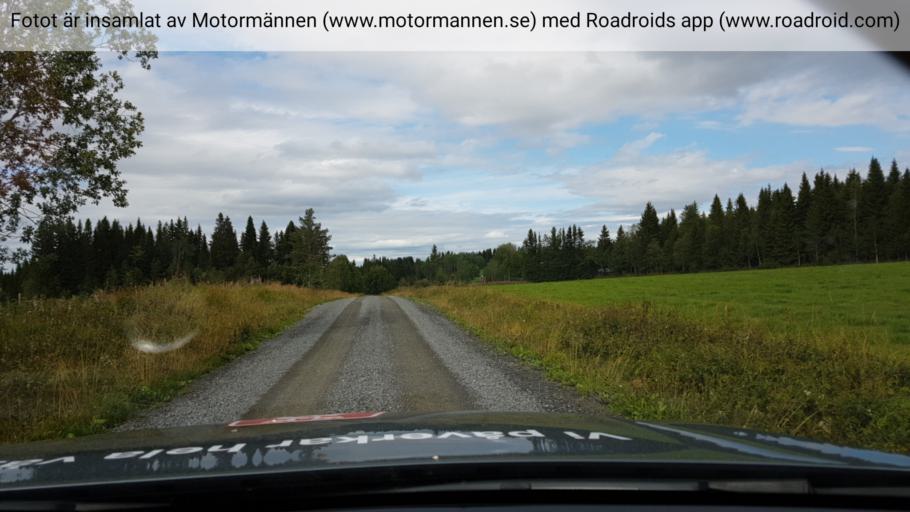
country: SE
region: Jaemtland
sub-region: Krokoms Kommun
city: Valla
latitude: 63.5219
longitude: 13.8894
